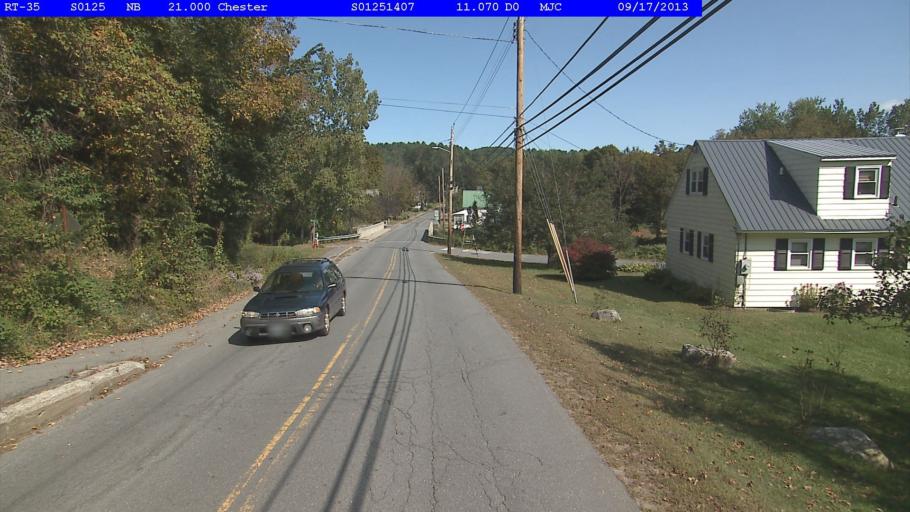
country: US
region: Vermont
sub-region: Windsor County
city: Chester
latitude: 43.2600
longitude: -72.5959
